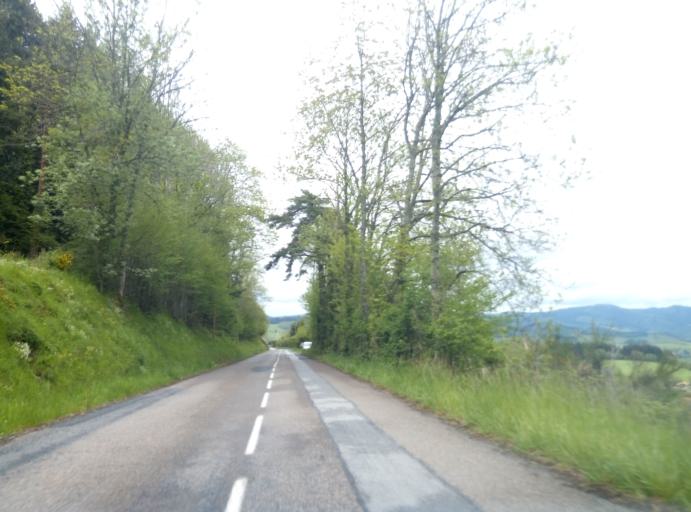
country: FR
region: Rhone-Alpes
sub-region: Departement du Rhone
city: Cublize
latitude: 45.9940
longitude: 4.4336
